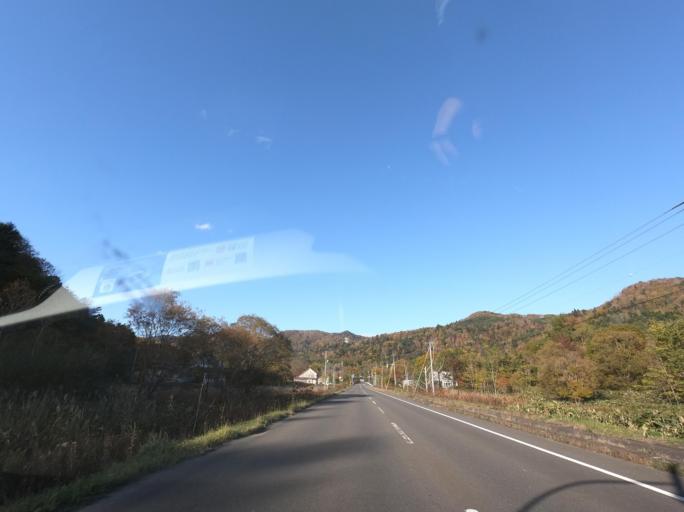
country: JP
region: Hokkaido
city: Iwamizawa
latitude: 43.0027
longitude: 142.0050
